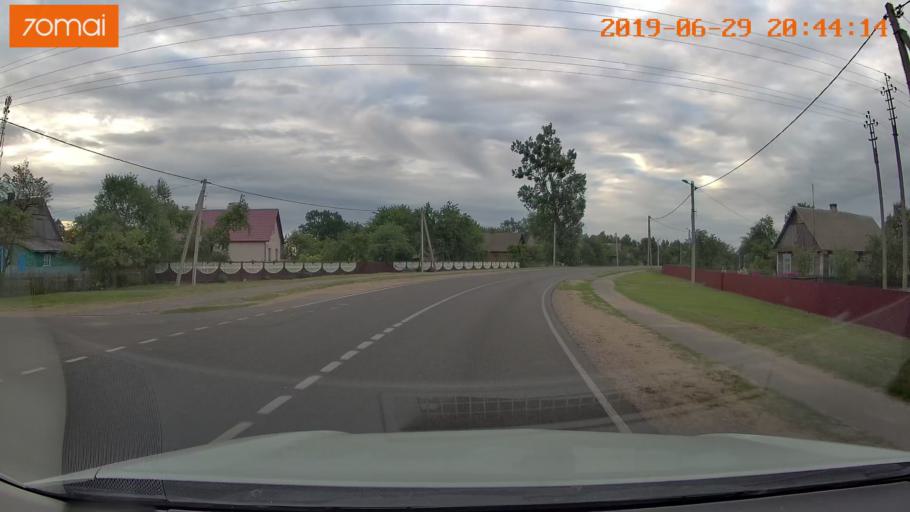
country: BY
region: Brest
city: Hantsavichy
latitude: 52.6116
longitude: 26.3076
